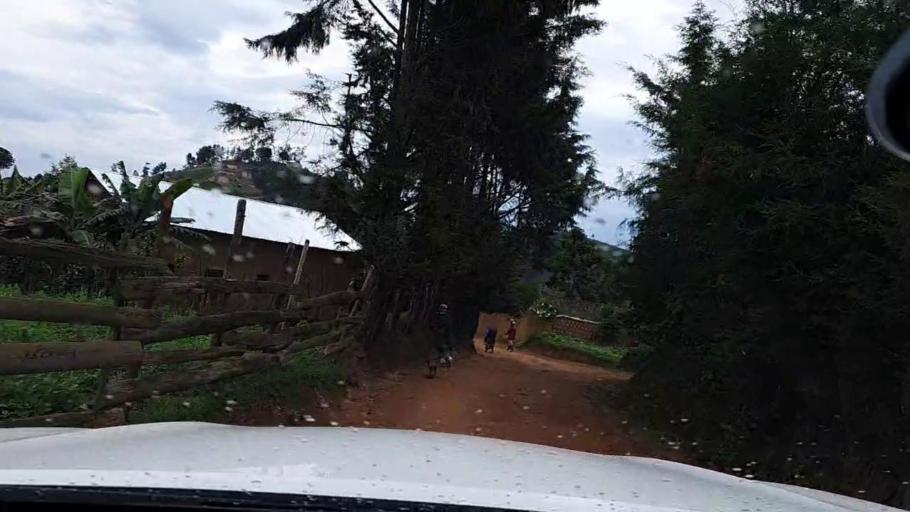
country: RW
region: Southern Province
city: Nzega
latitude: -2.3817
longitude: 29.2397
